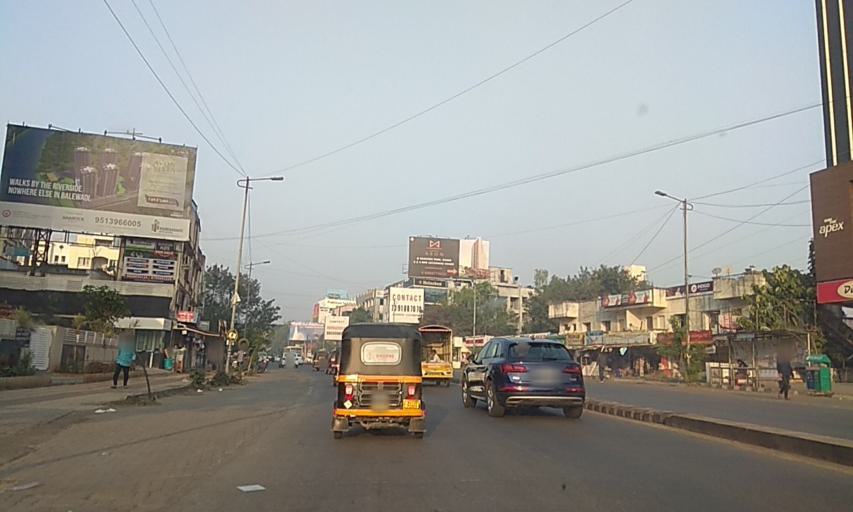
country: IN
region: Maharashtra
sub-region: Pune Division
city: Pimpri
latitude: 18.5640
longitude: 73.7813
